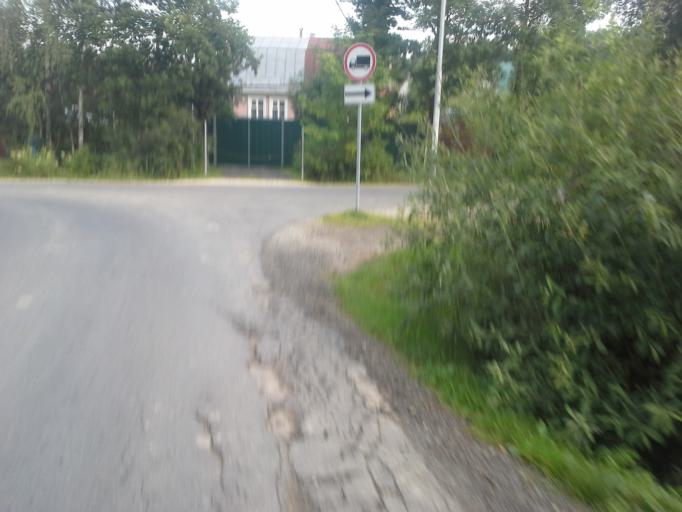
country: RU
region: Moskovskaya
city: Kievskij
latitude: 55.4626
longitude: 36.8859
